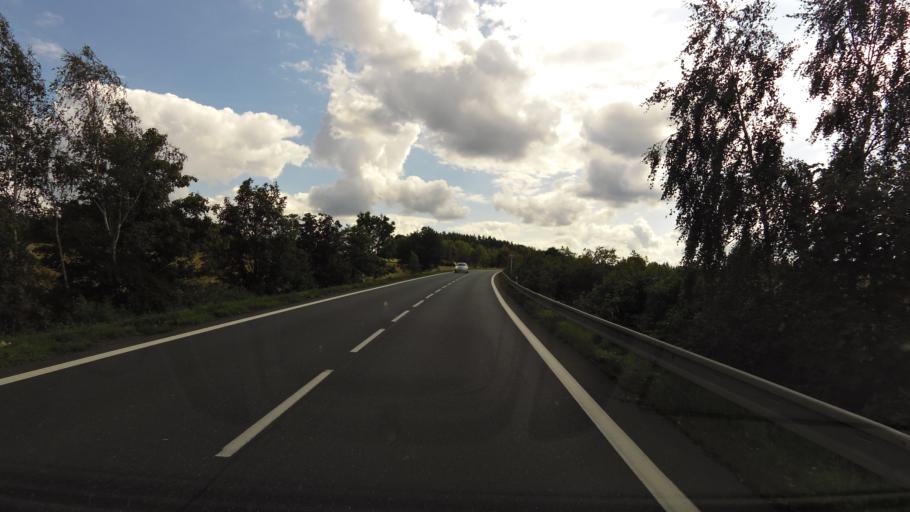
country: CZ
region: Plzensky
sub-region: Okres Domazlice
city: Domazlice
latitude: 49.4391
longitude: 12.8780
